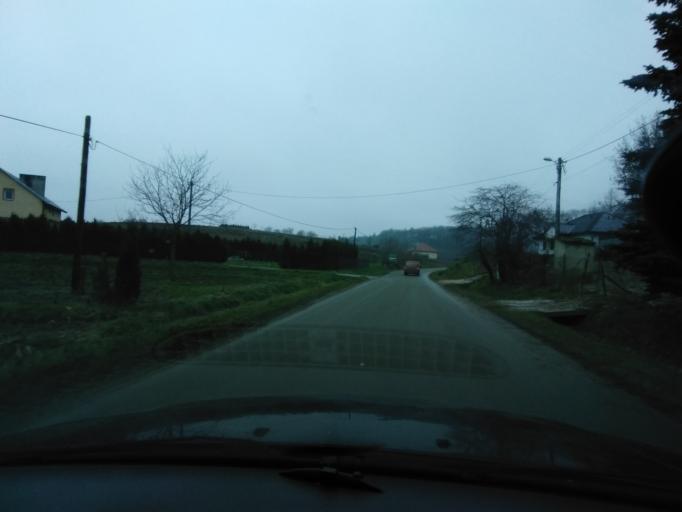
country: PL
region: Subcarpathian Voivodeship
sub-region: Powiat przeworski
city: Zarzecze
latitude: 49.9932
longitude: 22.5205
